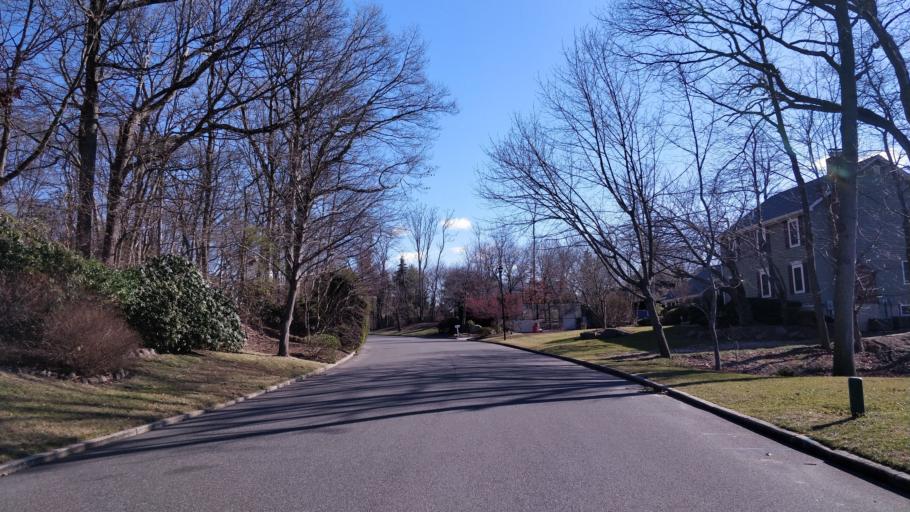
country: US
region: New York
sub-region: Suffolk County
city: Setauket-East Setauket
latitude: 40.9276
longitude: -73.0970
